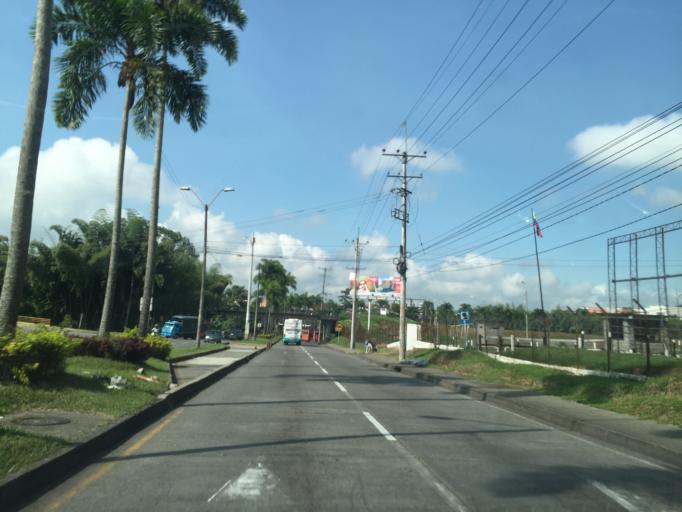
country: CO
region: Risaralda
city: Pereira
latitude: 4.8078
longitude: -75.7303
